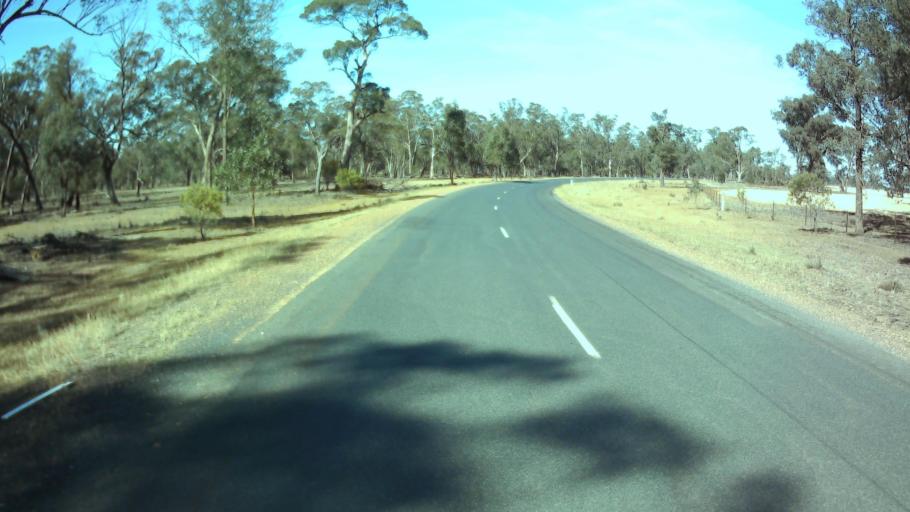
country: AU
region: New South Wales
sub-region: Weddin
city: Grenfell
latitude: -34.1344
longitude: 147.7901
